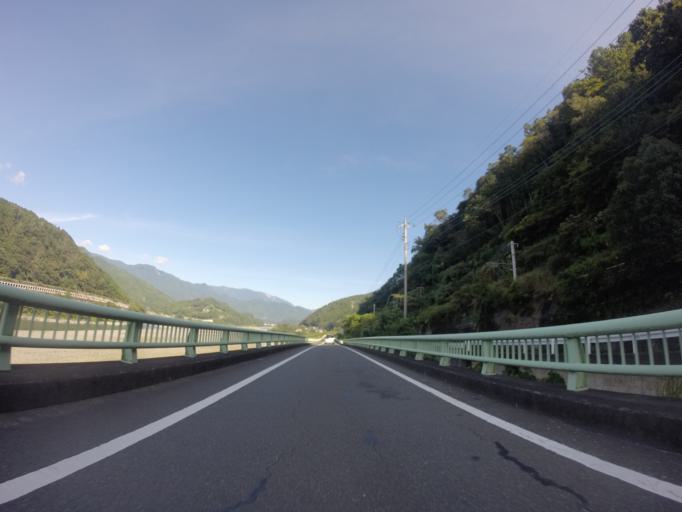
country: JP
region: Shizuoka
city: Fujinomiya
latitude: 35.2570
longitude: 138.4808
